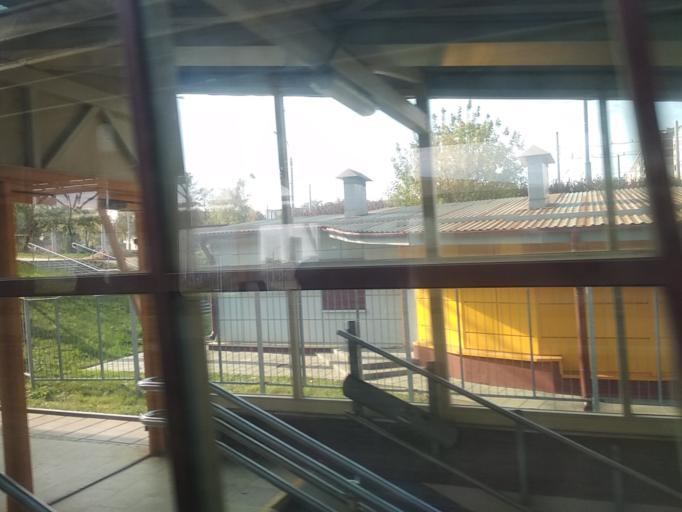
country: BY
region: Minsk
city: Syenitsa
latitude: 53.8512
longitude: 27.5564
